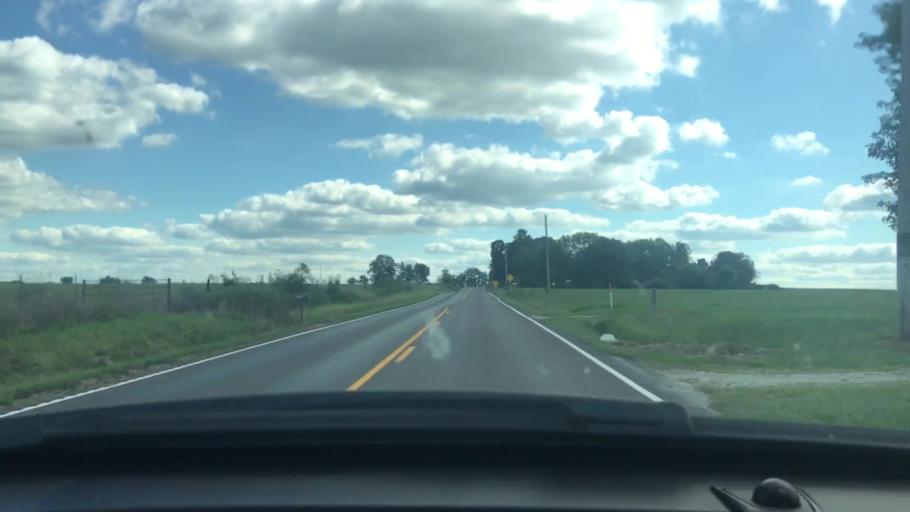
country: US
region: Missouri
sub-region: Wright County
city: Mountain Grove
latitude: 37.1692
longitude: -92.2672
